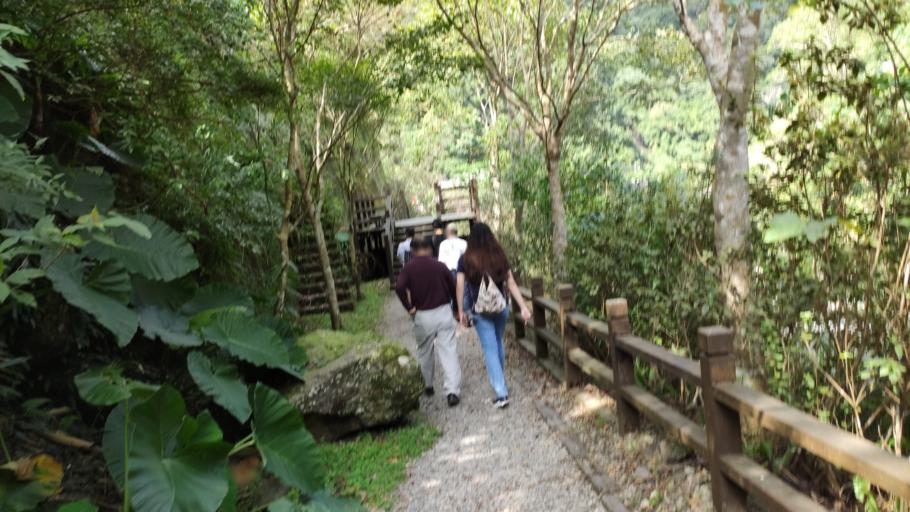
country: TW
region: Taiwan
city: Daxi
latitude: 24.8348
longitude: 121.4459
